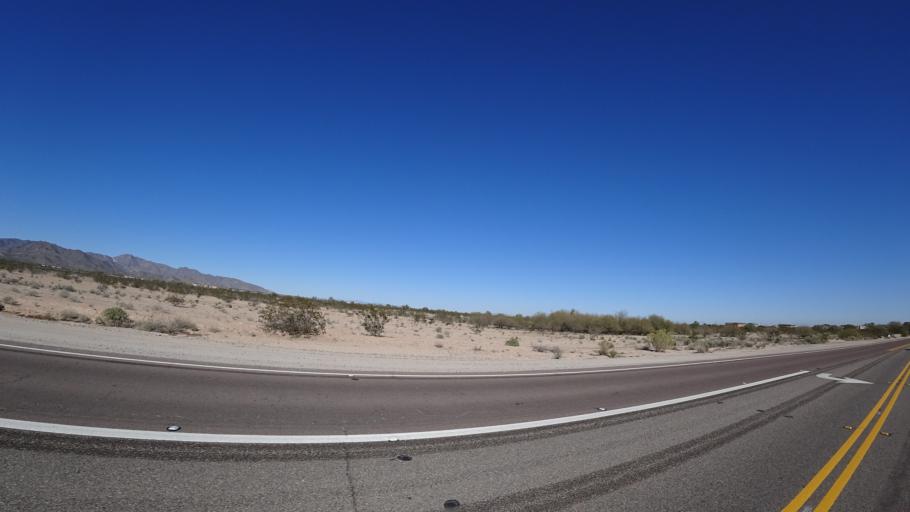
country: US
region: Arizona
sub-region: Maricopa County
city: Buckeye
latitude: 33.4356
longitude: -112.5020
